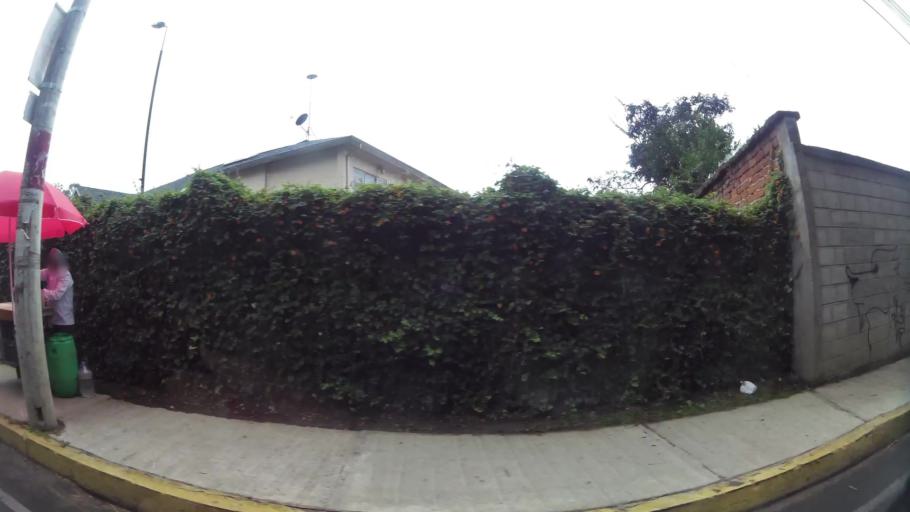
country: EC
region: Pichincha
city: Sangolqui
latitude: -0.2672
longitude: -78.4661
